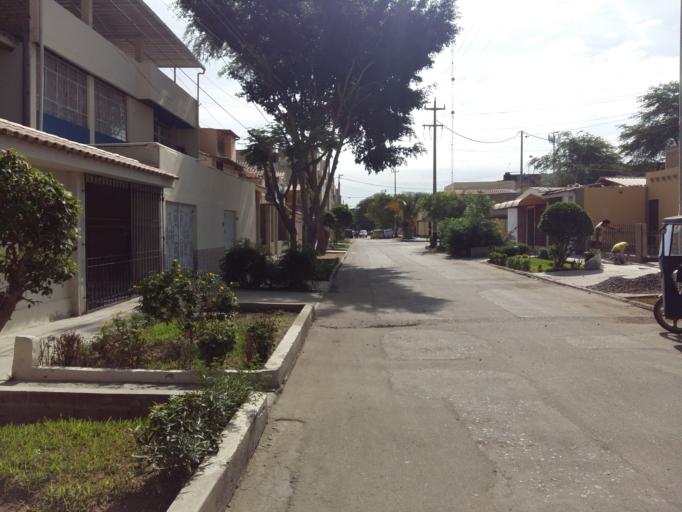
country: PE
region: Piura
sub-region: Provincia de Piura
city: Piura
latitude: -5.1887
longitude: -80.6205
